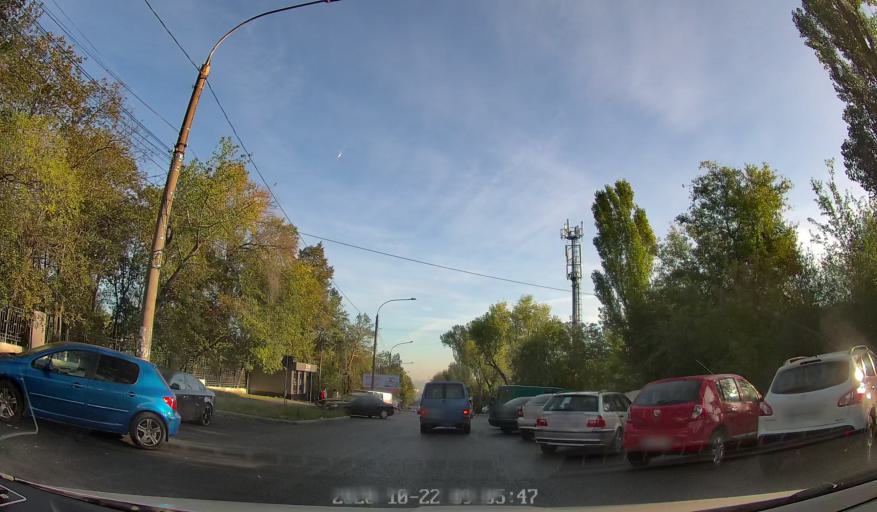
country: MD
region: Chisinau
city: Chisinau
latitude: 46.9913
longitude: 28.8281
